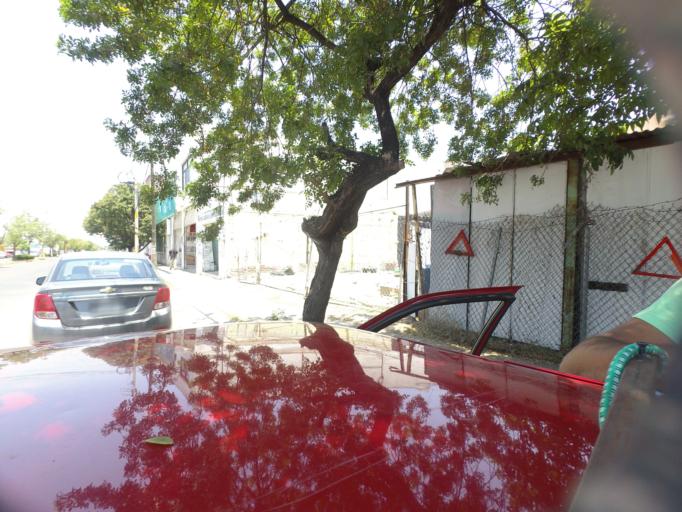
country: MX
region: Aguascalientes
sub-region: Aguascalientes
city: Aguascalientes
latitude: 21.8737
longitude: -102.2841
